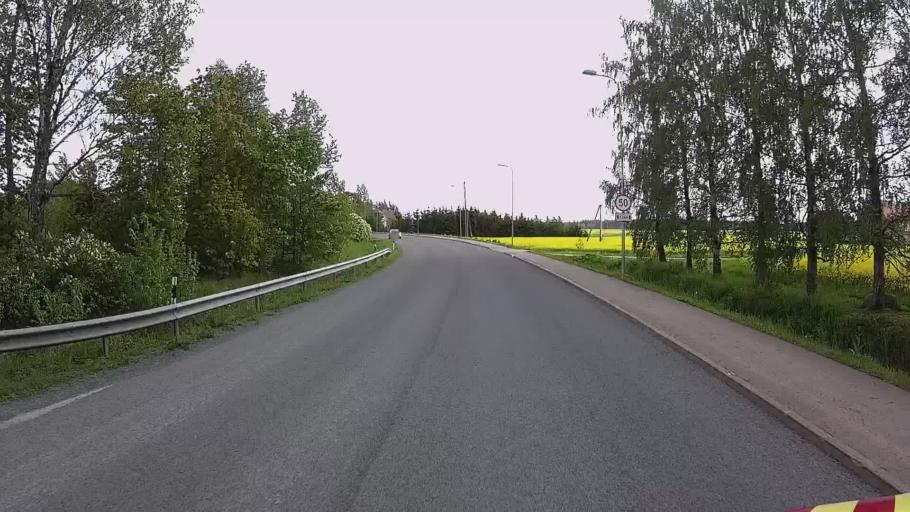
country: EE
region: Laeaene-Virumaa
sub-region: Vinni vald
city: Vinni
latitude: 59.1560
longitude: 26.5884
